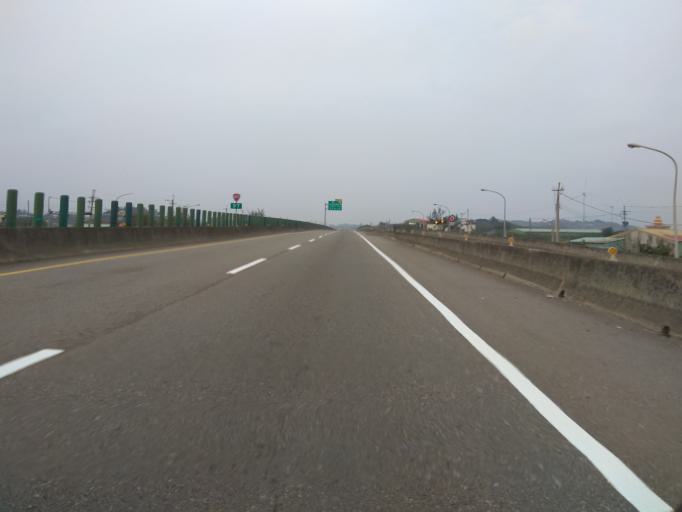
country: TW
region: Taiwan
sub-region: Miaoli
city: Miaoli
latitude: 24.6607
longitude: 120.8160
